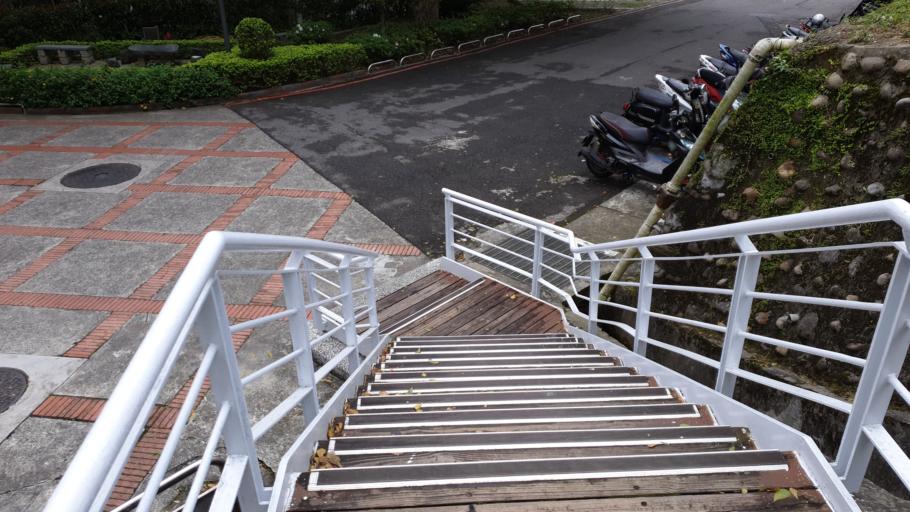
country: TW
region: Taipei
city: Taipei
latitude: 25.0930
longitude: 121.5467
